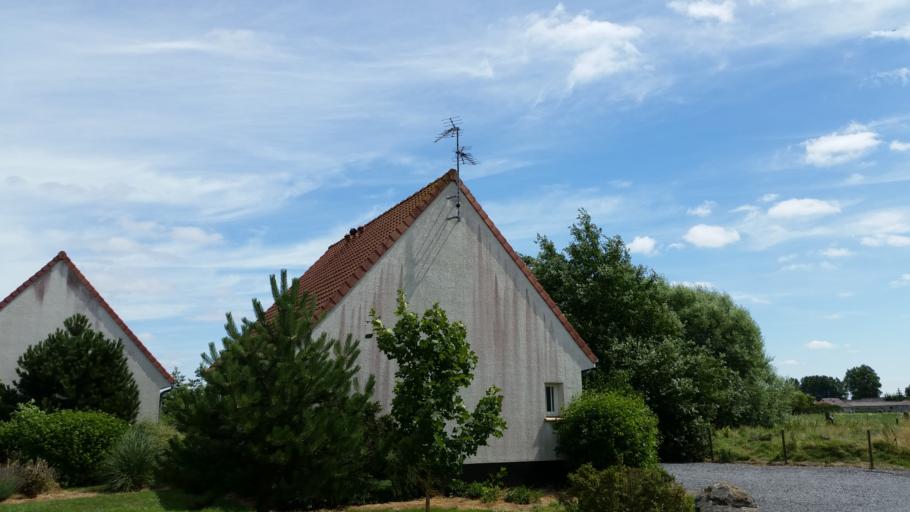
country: FR
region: Nord-Pas-de-Calais
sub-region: Departement du Pas-de-Calais
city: Oye-Plage
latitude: 50.9365
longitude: 2.0143
